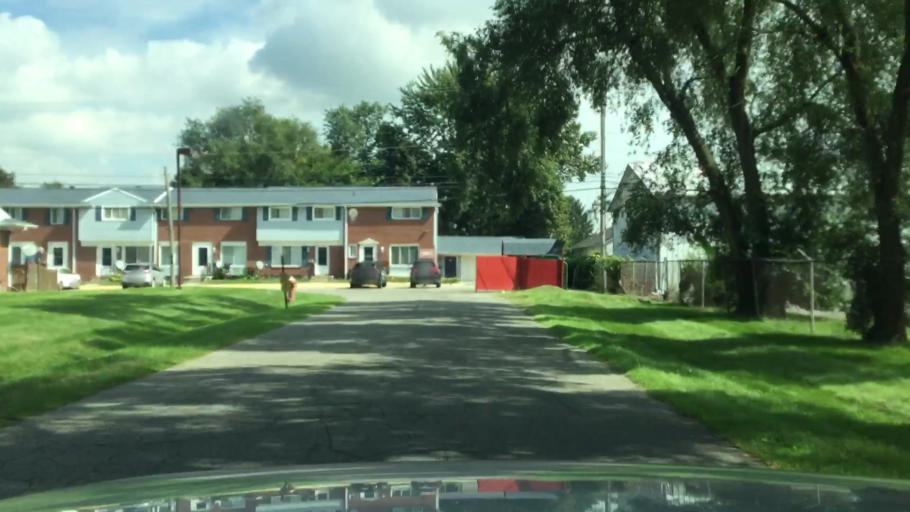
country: US
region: Michigan
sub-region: Wayne County
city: Romulus
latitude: 42.2413
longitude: -83.3878
